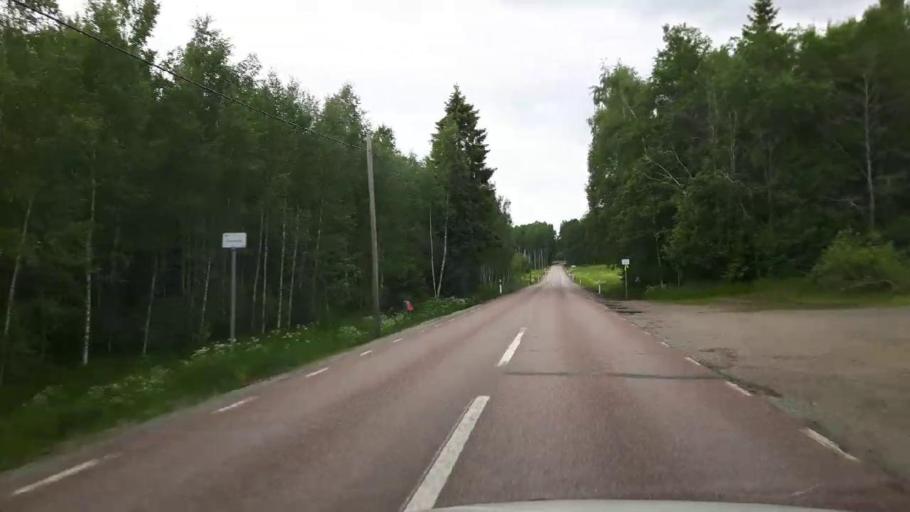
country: SE
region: Vaestmanland
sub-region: Kopings Kommun
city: Kolsva
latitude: 59.7093
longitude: 15.7981
